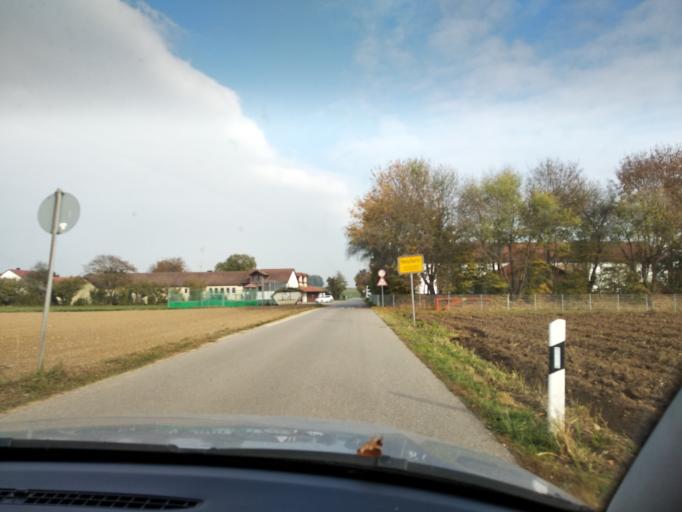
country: DE
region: Bavaria
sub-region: Upper Bavaria
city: Poing
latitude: 48.1447
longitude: 11.8151
